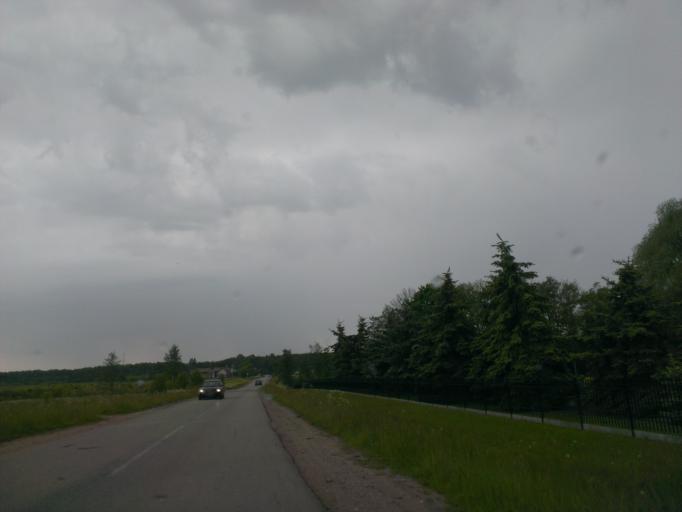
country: LT
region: Klaipedos apskritis
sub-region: Klaipeda
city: Klaipeda
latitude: 55.8052
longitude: 21.0757
